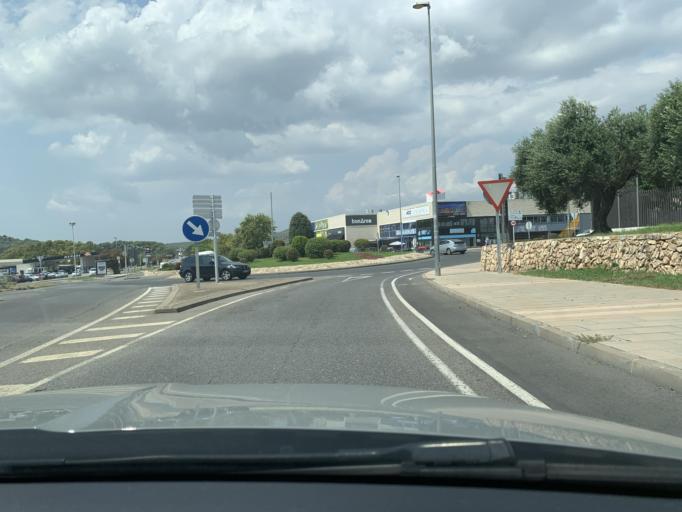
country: ES
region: Catalonia
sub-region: Provincia de Tarragona
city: Altafulla
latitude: 41.1403
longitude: 1.3681
